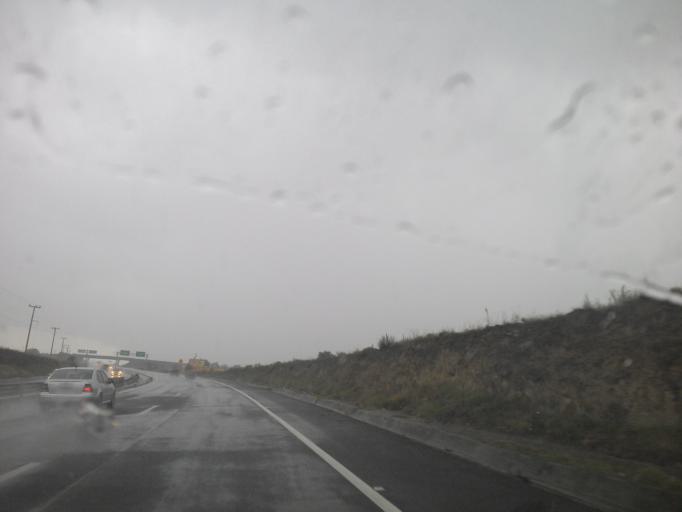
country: MX
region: Morelos
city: Nopaltepec
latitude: 19.8449
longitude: -98.6873
